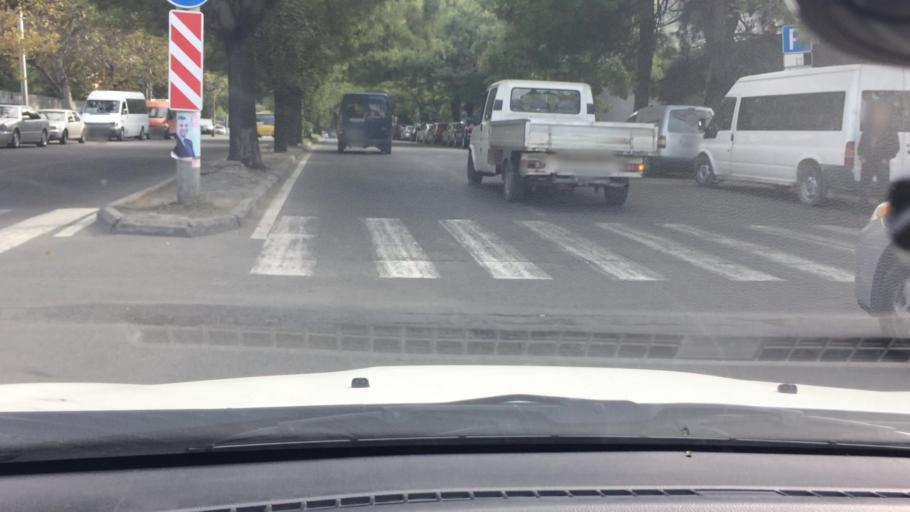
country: GE
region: T'bilisi
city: Tbilisi
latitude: 41.6749
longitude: 44.8300
